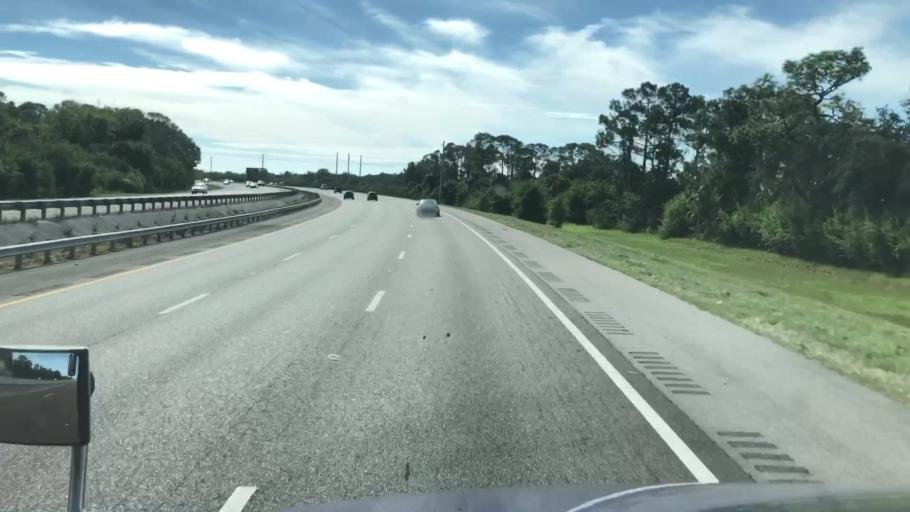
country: US
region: Florida
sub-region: Brevard County
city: Port Saint John
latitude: 28.5192
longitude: -80.8518
